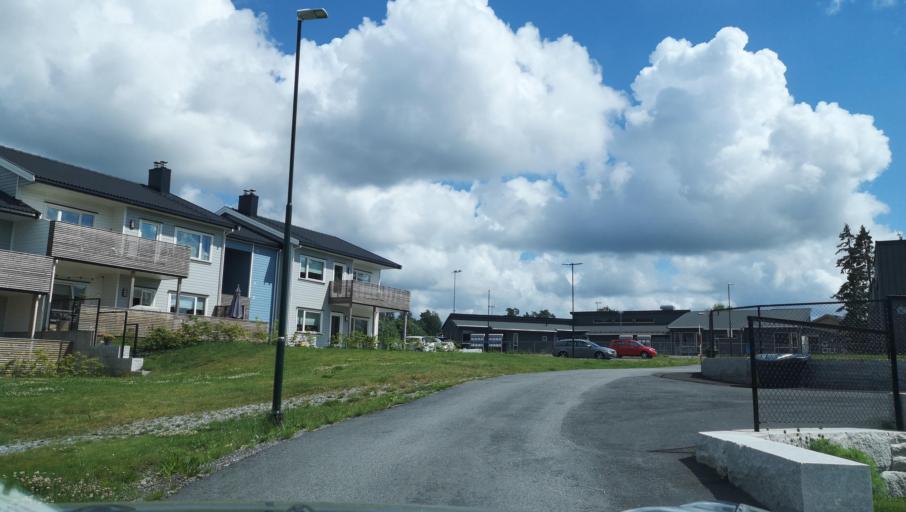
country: NO
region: Ostfold
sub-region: Hobol
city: Tomter
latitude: 59.6651
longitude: 10.9961
